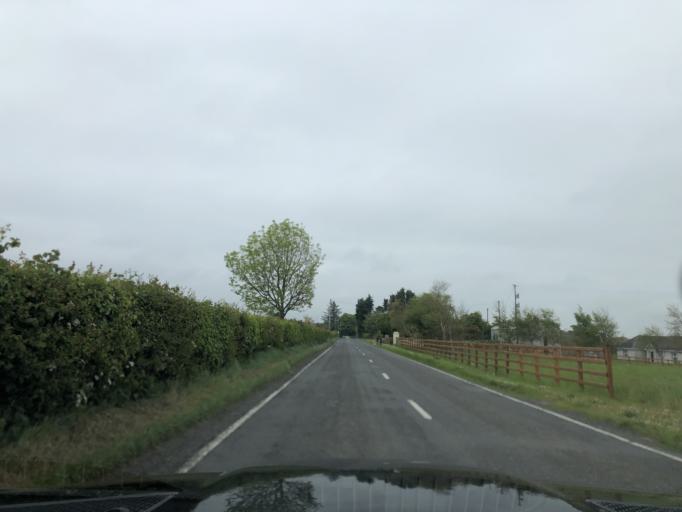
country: GB
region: Northern Ireland
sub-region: Down District
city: Portaferry
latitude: 54.3577
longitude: -5.5762
